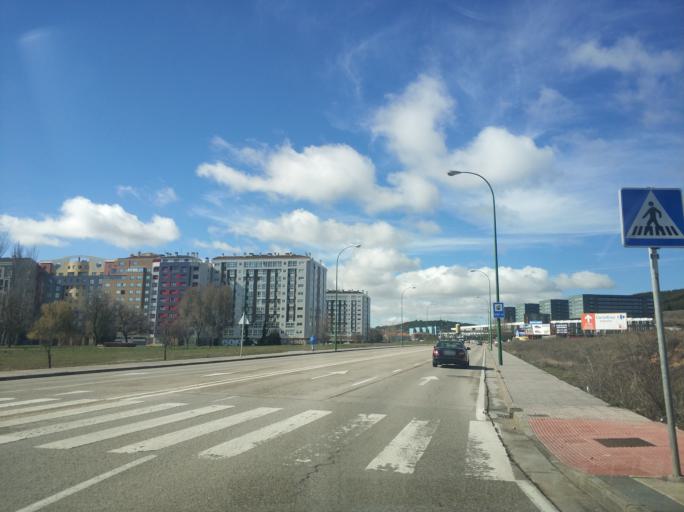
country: ES
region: Castille and Leon
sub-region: Provincia de Burgos
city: Burgos
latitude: 42.3648
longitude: -3.6774
